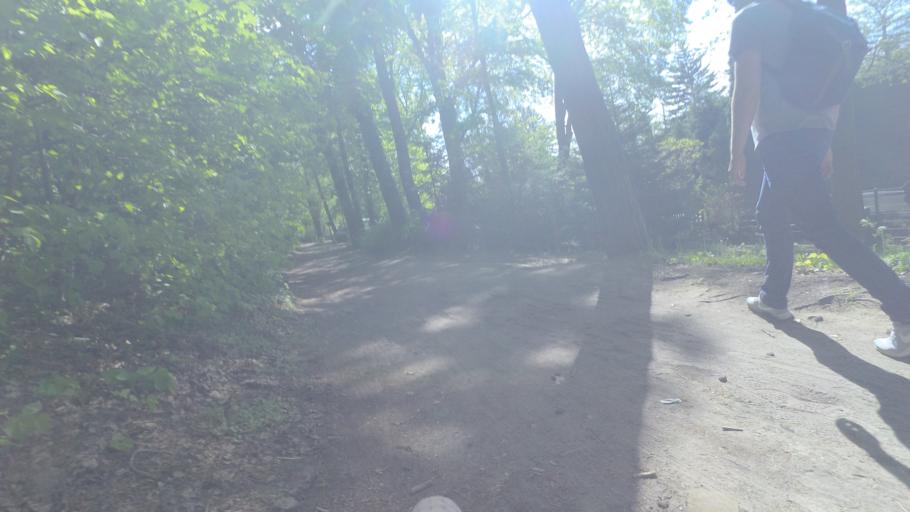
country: DE
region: Brandenburg
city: Erkner
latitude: 52.4235
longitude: 13.7637
